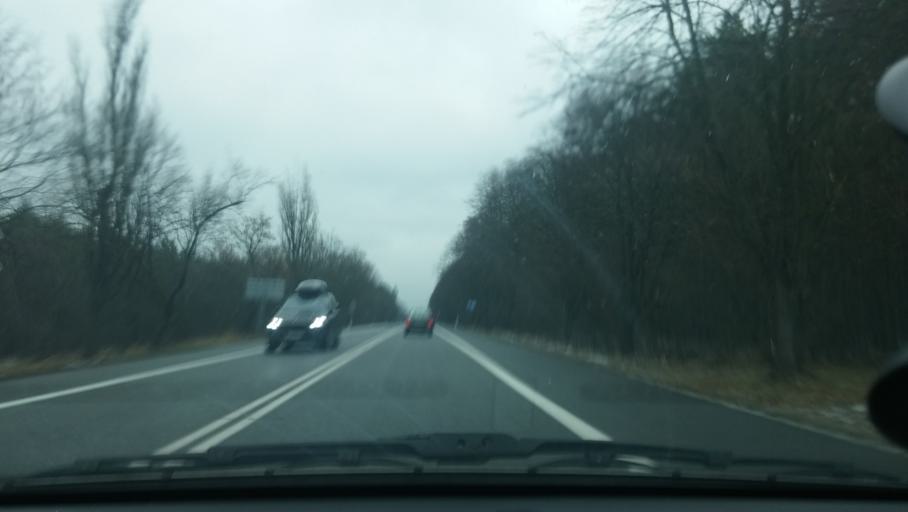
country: PL
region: Masovian Voivodeship
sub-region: Powiat minski
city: Kaluszyn
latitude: 52.2098
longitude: 21.8643
